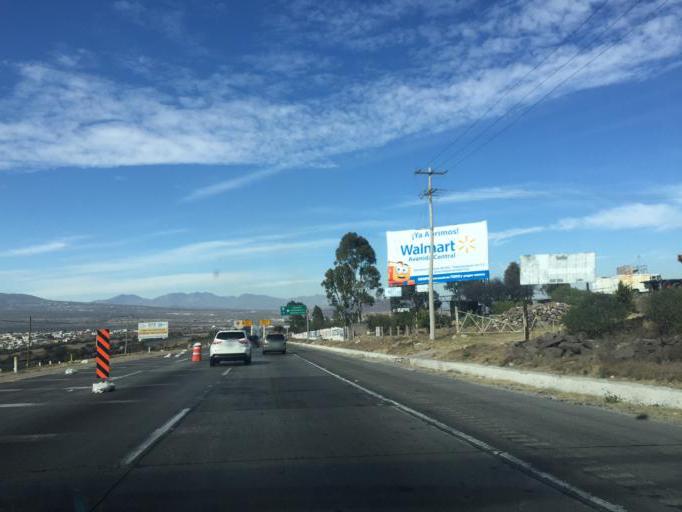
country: MX
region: Queretaro
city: San Juan del Rio
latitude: 20.3626
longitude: -99.9690
